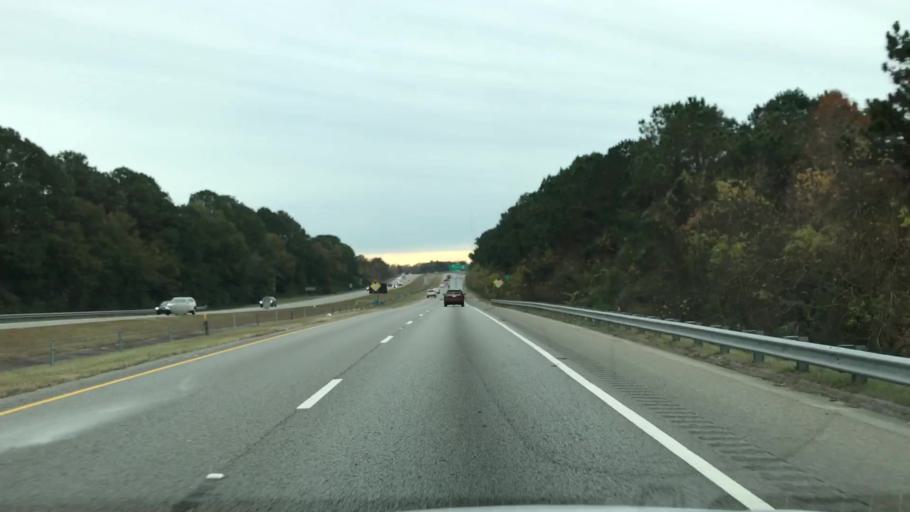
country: US
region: South Carolina
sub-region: Charleston County
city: Mount Pleasant
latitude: 32.8297
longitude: -79.8521
